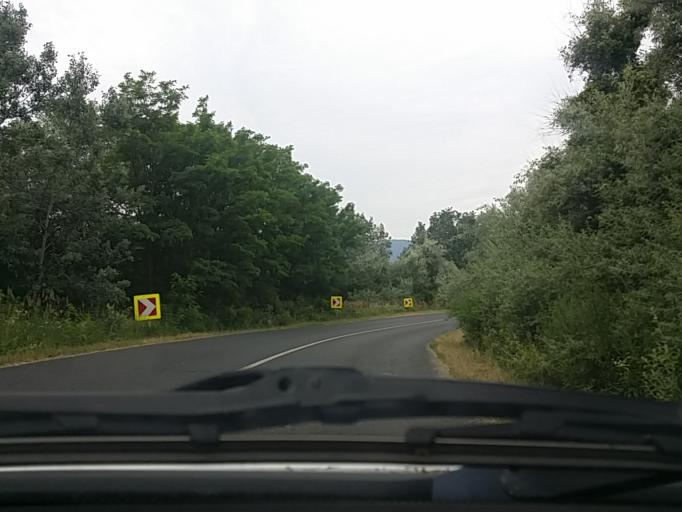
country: HU
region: Pest
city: Csobanka
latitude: 47.6262
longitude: 18.9520
